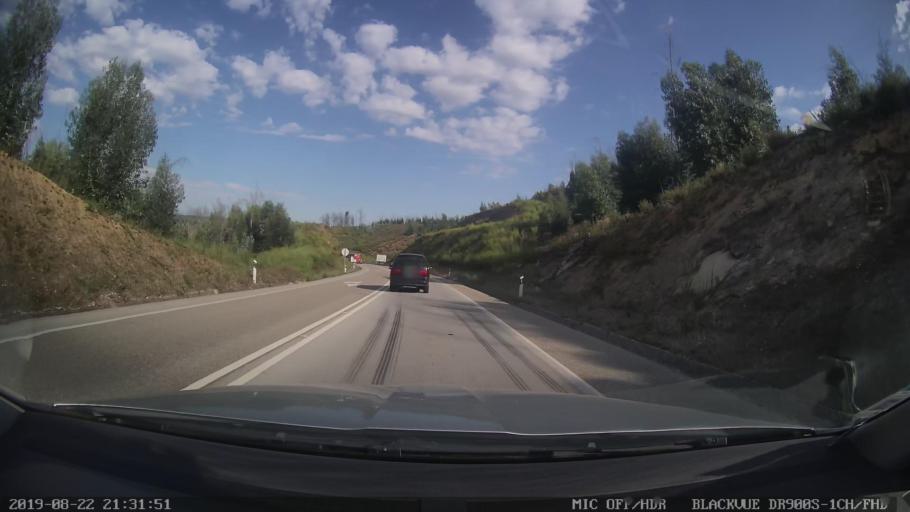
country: PT
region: Leiria
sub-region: Pedrogao Grande
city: Pedrogao Grande
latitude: 39.9241
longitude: -8.1571
